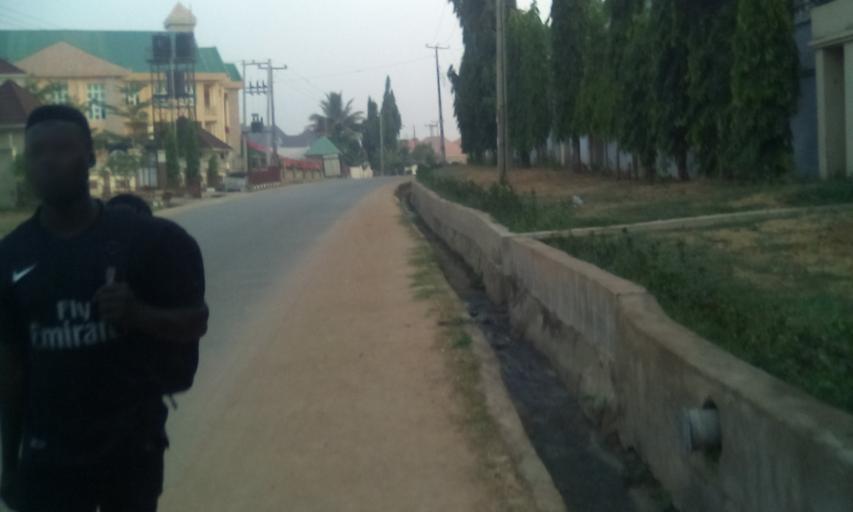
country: NG
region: Abuja Federal Capital Territory
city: Abuja
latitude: 8.9863
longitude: 7.3541
